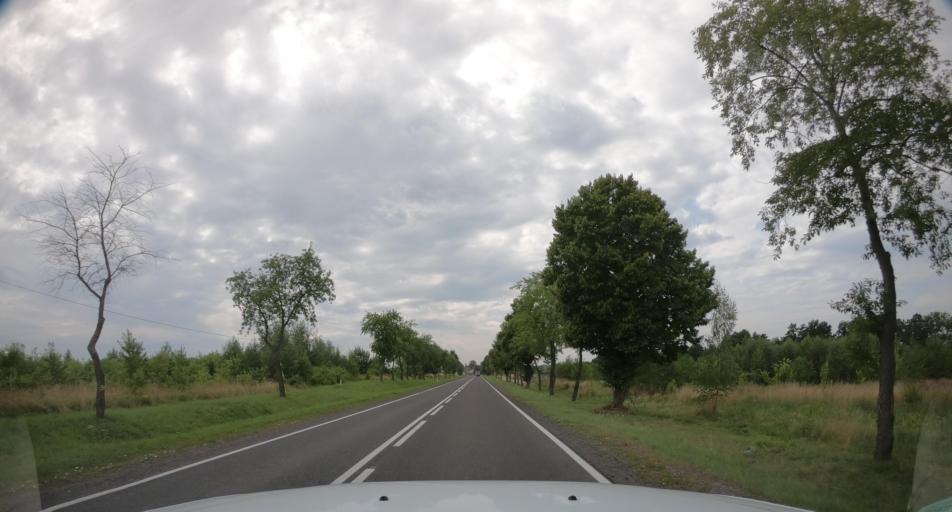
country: PL
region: West Pomeranian Voivodeship
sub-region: Powiat walecki
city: Walcz
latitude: 53.2466
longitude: 16.3969
